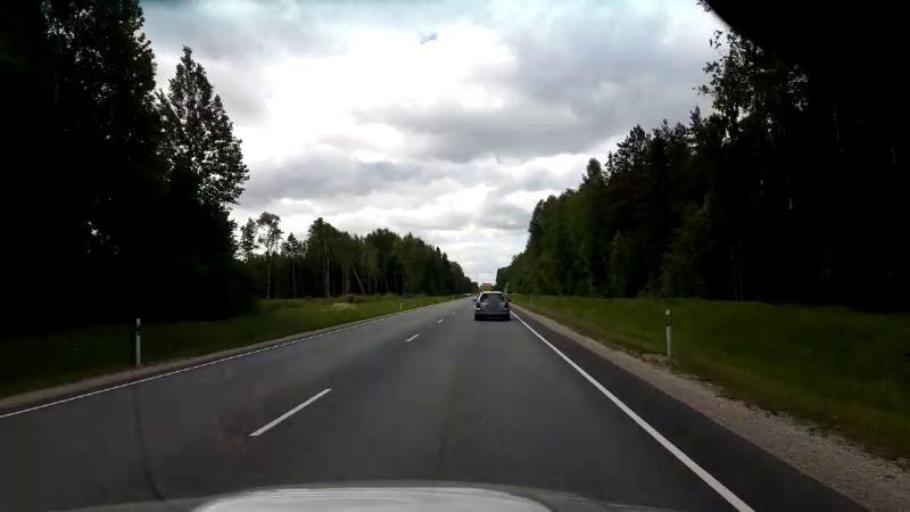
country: EE
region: Raplamaa
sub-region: Maerjamaa vald
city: Marjamaa
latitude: 58.7901
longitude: 24.4130
